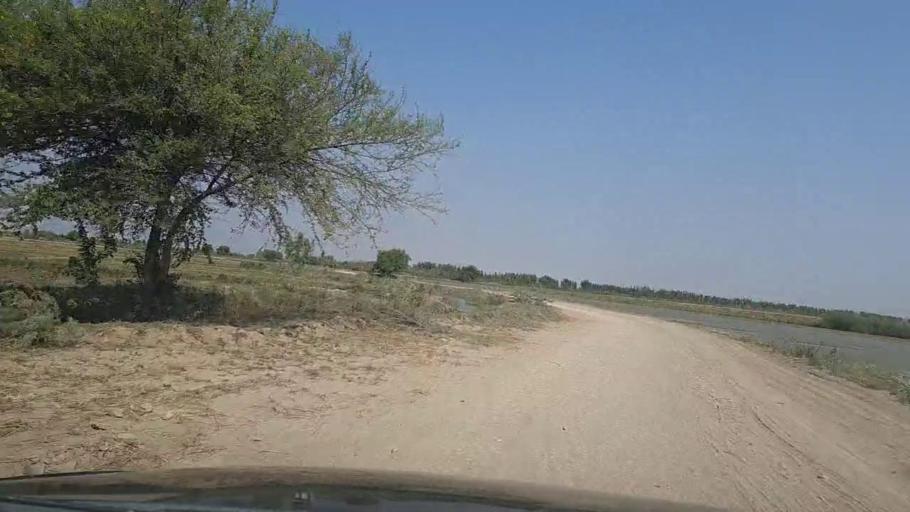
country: PK
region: Sindh
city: Thatta
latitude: 24.6270
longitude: 67.8137
